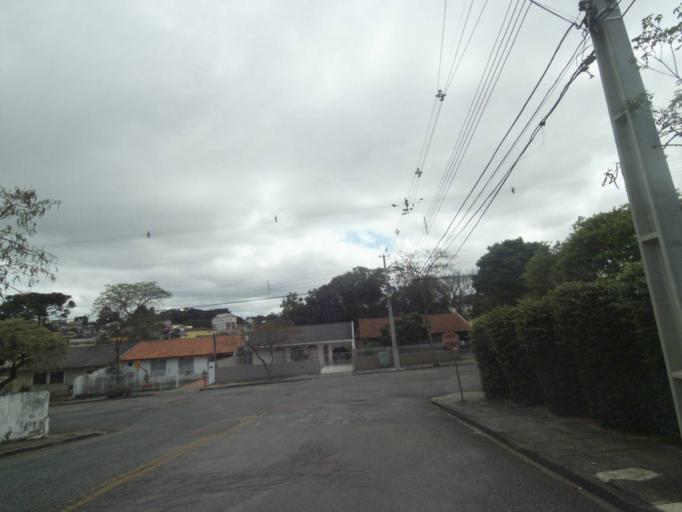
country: BR
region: Parana
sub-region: Pinhais
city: Pinhais
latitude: -25.3946
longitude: -49.2150
